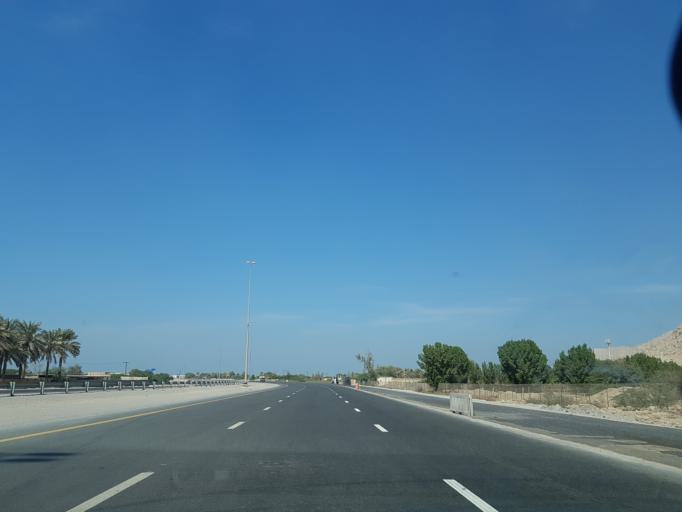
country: AE
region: Ra's al Khaymah
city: Ras al-Khaimah
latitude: 25.8234
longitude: 56.0233
